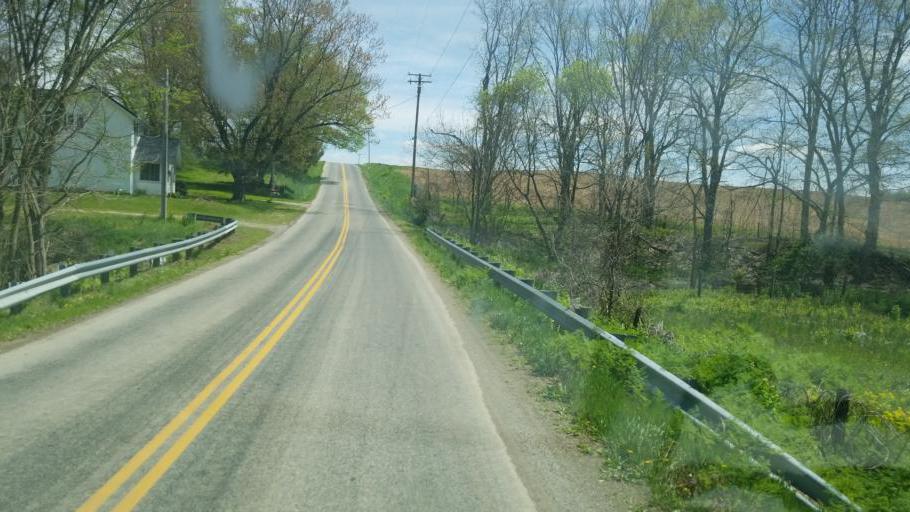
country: US
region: Ohio
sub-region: Ashland County
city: Loudonville
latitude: 40.7597
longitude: -82.1539
